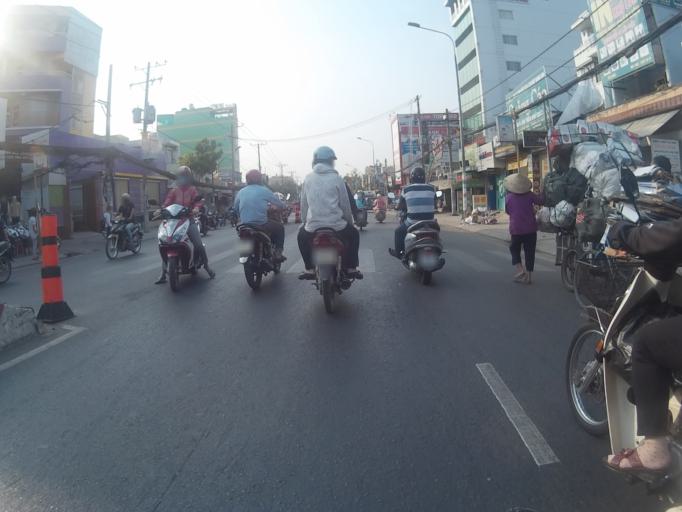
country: VN
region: Ho Chi Minh City
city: Ho Chi Minh City
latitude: 10.8447
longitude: 106.6397
